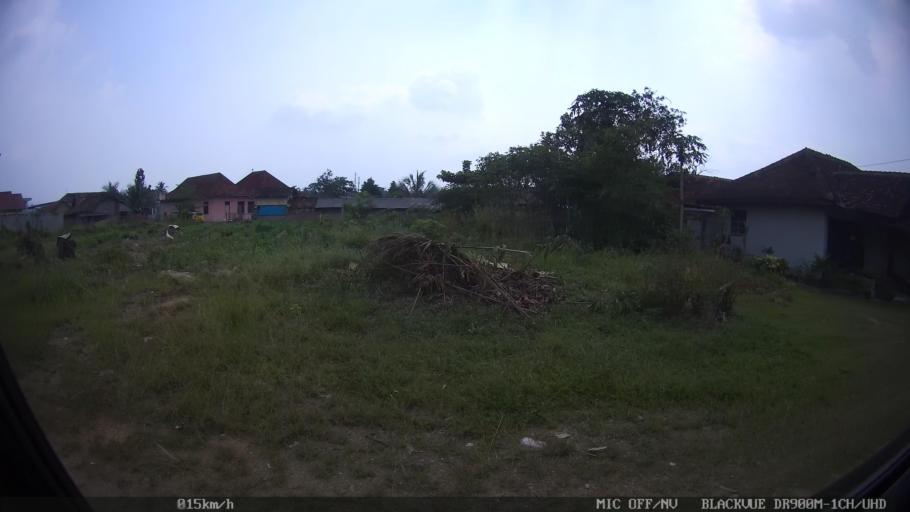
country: ID
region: Lampung
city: Gadingrejo
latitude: -5.3725
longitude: 105.0689
